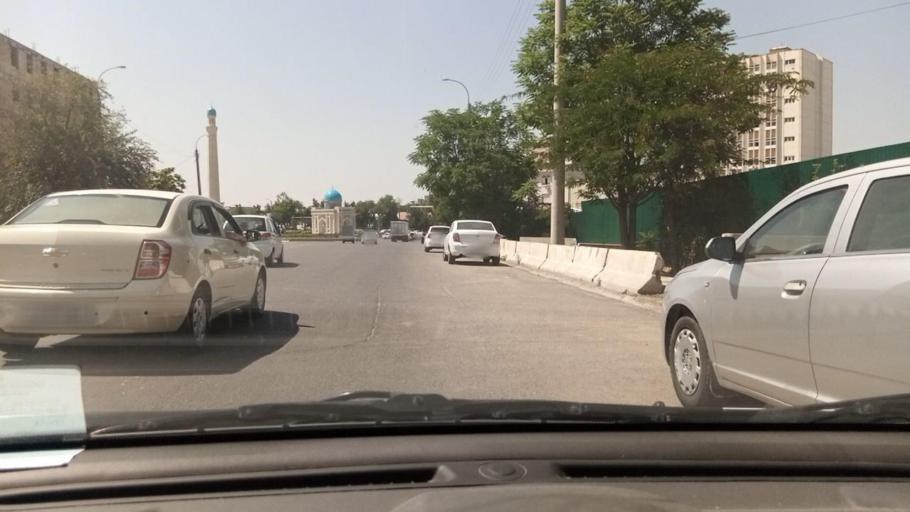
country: UZ
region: Toshkent Shahri
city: Tashkent
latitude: 41.2585
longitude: 69.1901
